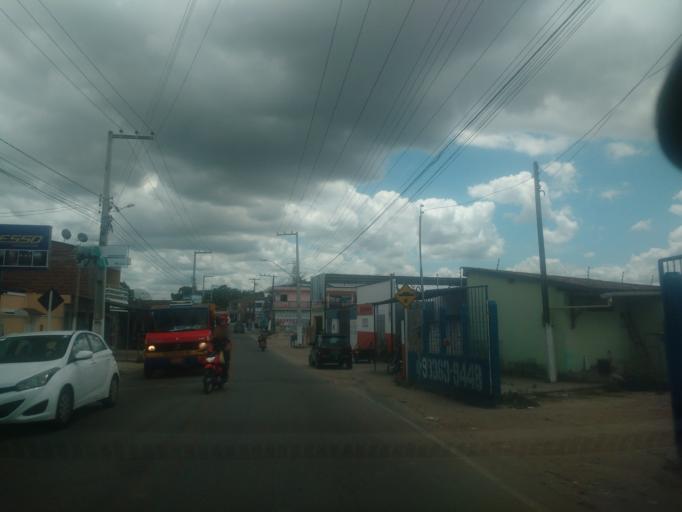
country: BR
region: Alagoas
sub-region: Uniao Dos Palmares
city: Uniao dos Palmares
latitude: -9.1533
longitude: -36.0214
